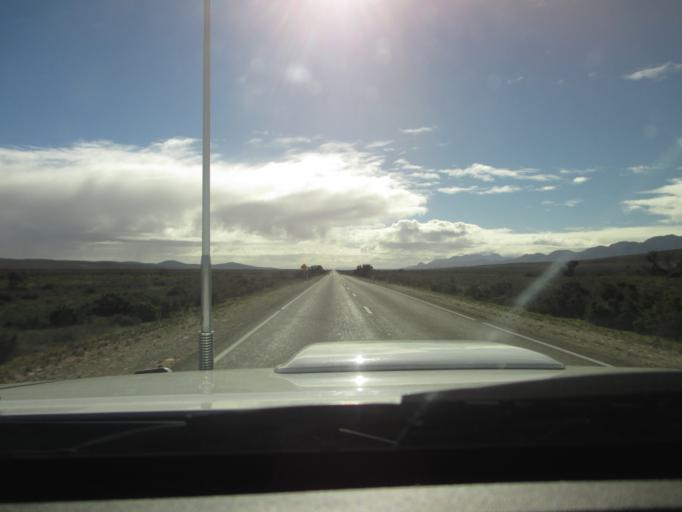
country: AU
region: South Australia
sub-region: Flinders Ranges
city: Quorn
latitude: -31.7239
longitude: 138.3462
